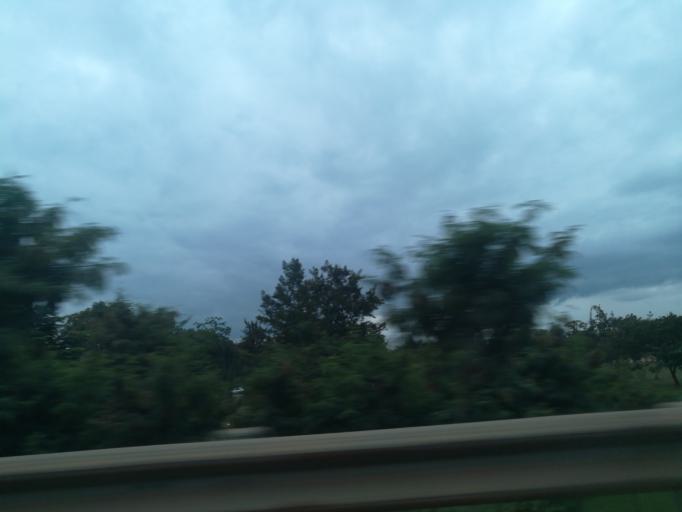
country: KE
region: Nairobi Area
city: Thika
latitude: -1.0412
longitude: 37.0637
